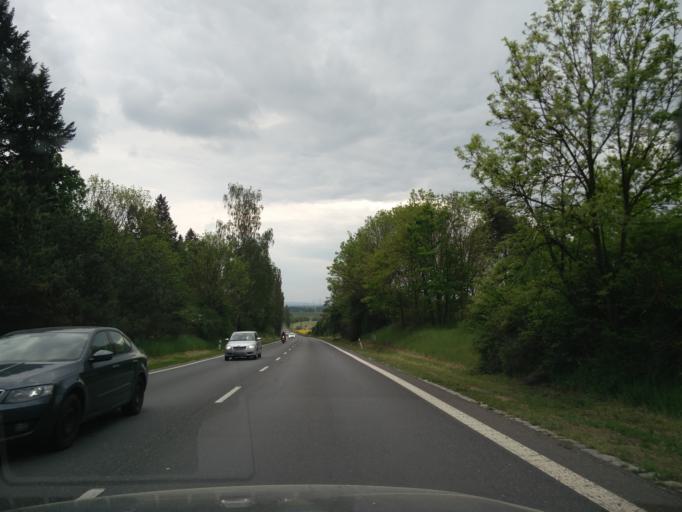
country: CZ
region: Jihocesky
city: Mirovice
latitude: 49.5453
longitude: 14.0815
